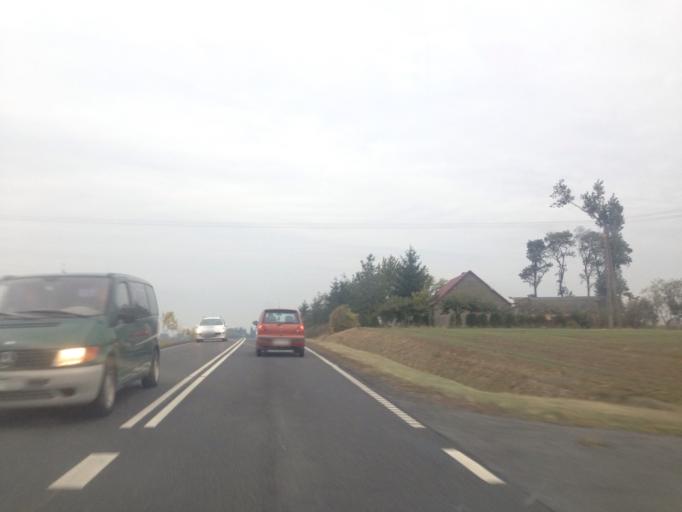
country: PL
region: Kujawsko-Pomorskie
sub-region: Powiat mogilenski
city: Mogilno
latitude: 52.6165
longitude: 17.9579
